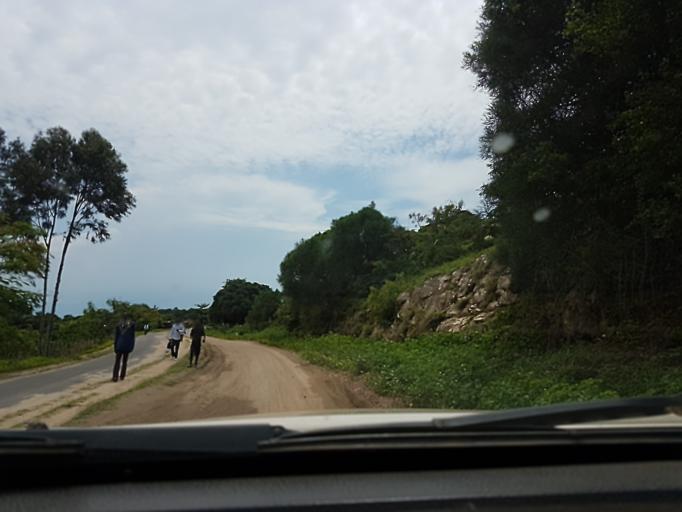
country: CD
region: South Kivu
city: Uvira
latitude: -3.2425
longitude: 29.1605
